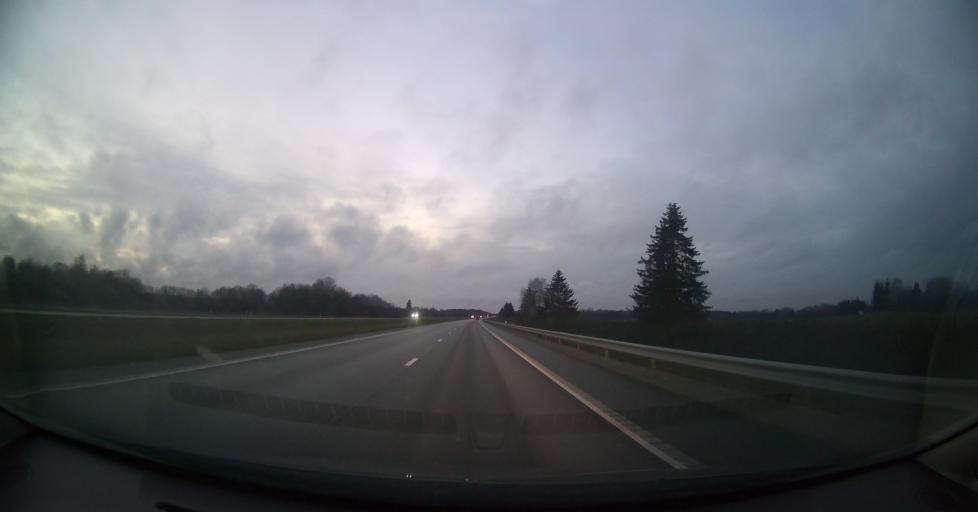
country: EE
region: Laeaene-Virumaa
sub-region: Kadrina vald
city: Kadrina
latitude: 59.4401
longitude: 26.1167
